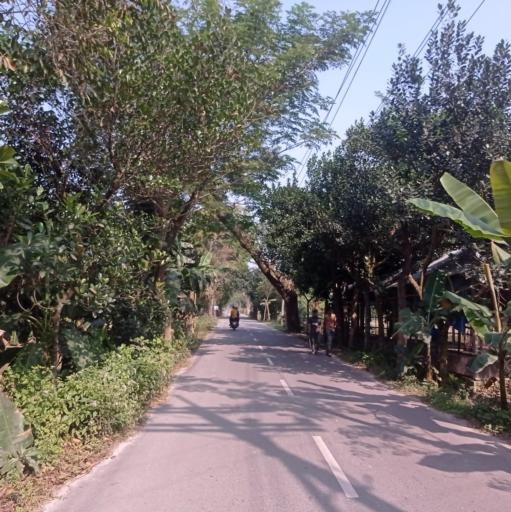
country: BD
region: Dhaka
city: Narsingdi
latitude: 24.0597
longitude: 90.6873
